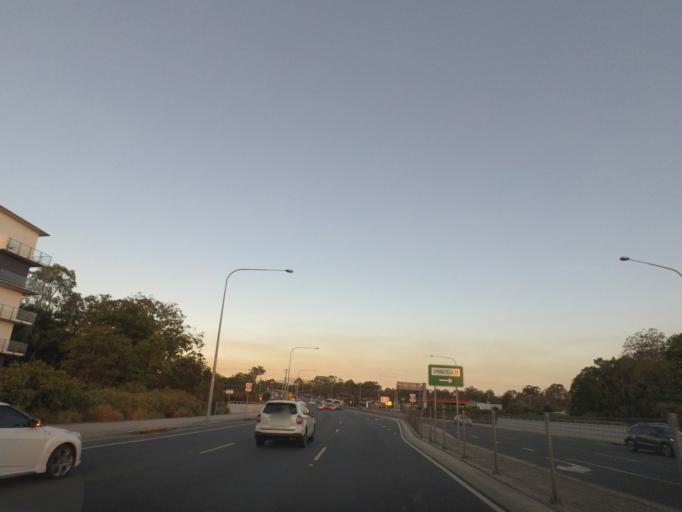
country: AU
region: Queensland
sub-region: Brisbane
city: Nathan
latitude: -27.5619
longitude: 153.0729
